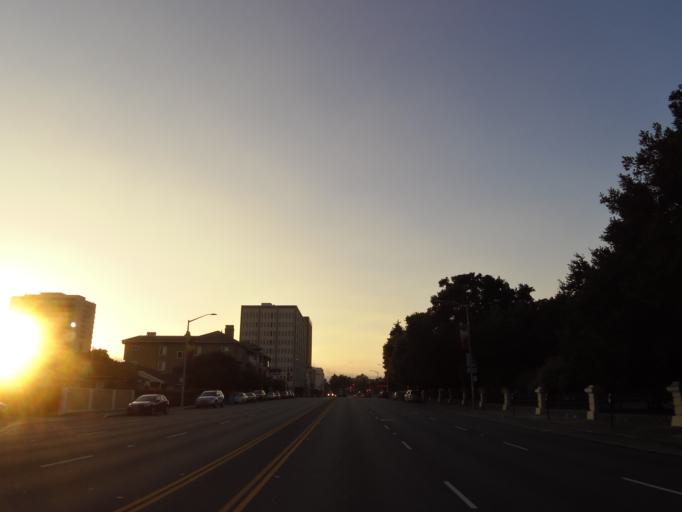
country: US
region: California
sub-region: San Mateo County
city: San Mateo
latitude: 37.5598
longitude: -122.3225
